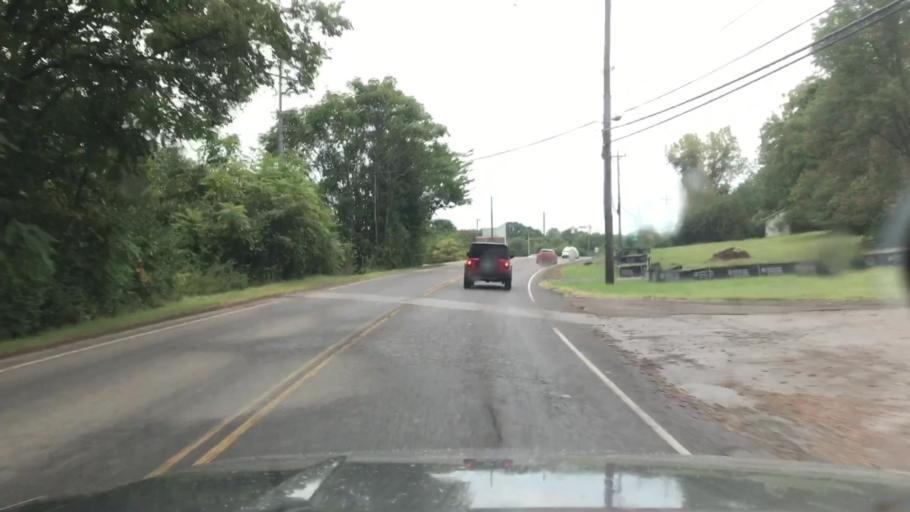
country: US
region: Tennessee
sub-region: Davidson County
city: Lakewood
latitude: 36.1788
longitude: -86.6179
